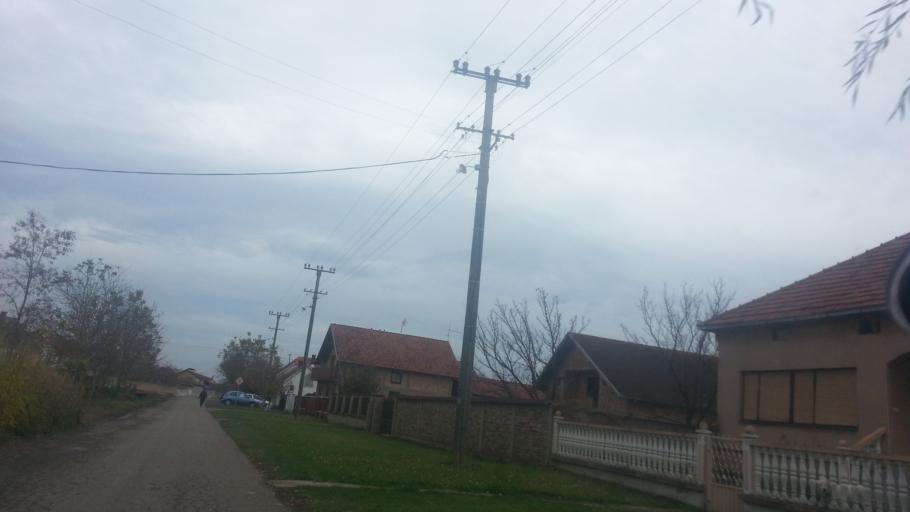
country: RS
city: Golubinci
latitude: 44.9882
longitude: 20.0716
